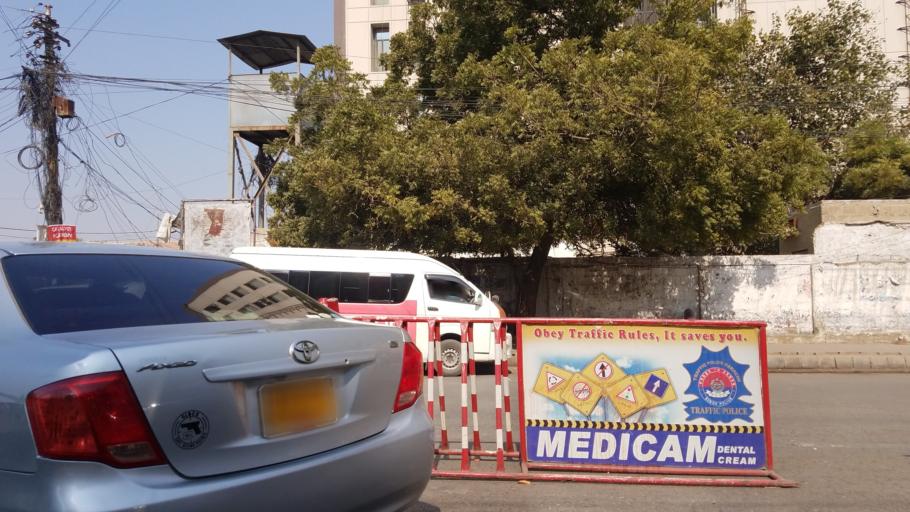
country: PK
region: Sindh
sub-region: Karachi District
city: Karachi
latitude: 24.8506
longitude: 67.0161
